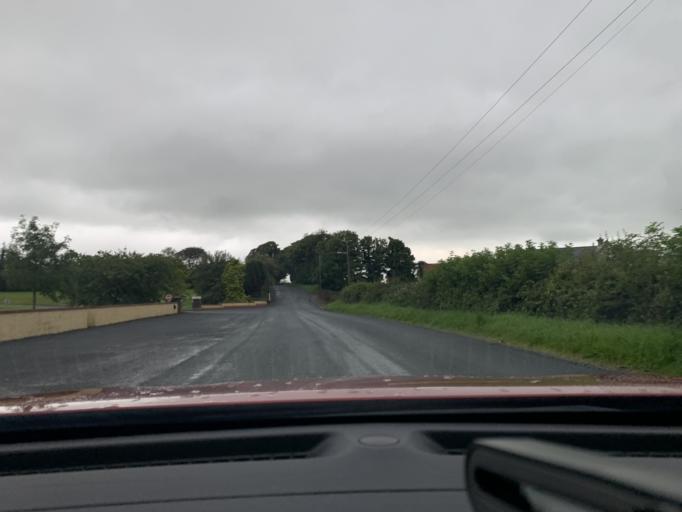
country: IE
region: Connaught
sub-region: Sligo
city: Sligo
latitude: 54.3050
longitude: -8.5135
